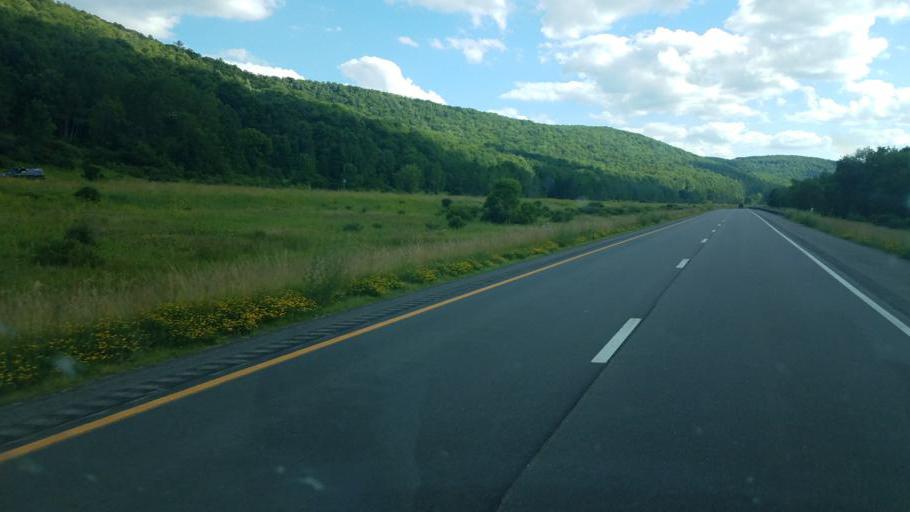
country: US
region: New York
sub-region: Allegany County
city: Cuba
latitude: 42.2027
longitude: -78.3297
